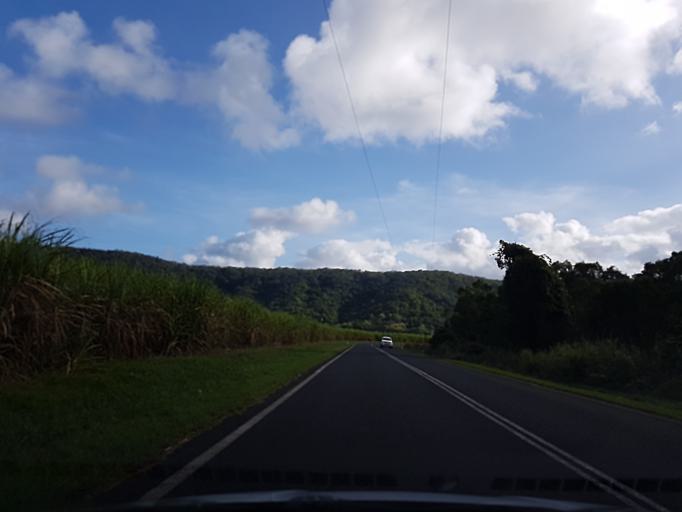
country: AU
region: Queensland
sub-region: Cairns
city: Port Douglas
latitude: -16.2783
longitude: 145.3835
